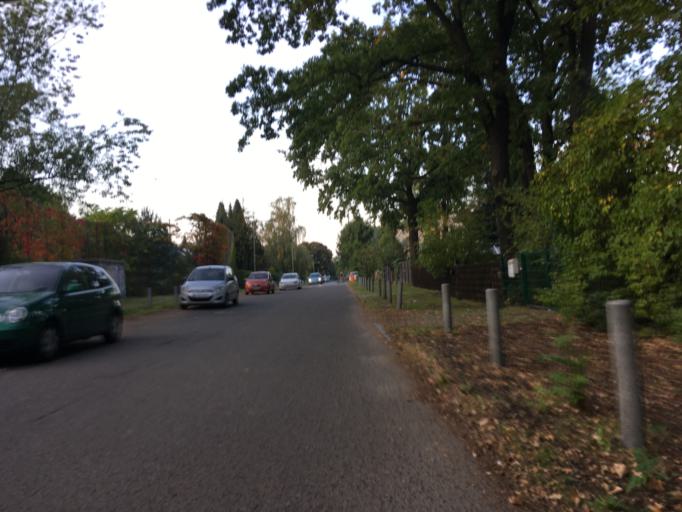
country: DE
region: Berlin
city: Biesdorf
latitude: 52.4906
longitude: 13.5584
